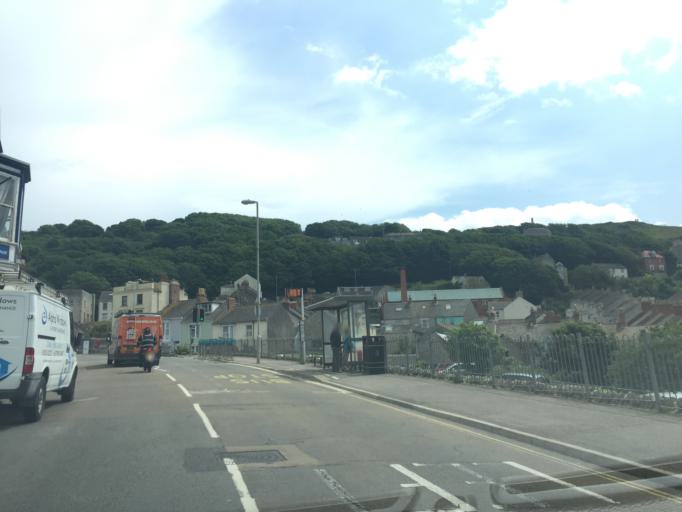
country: GB
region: England
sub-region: Dorset
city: Fortuneswell
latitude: 50.5592
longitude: -2.4423
